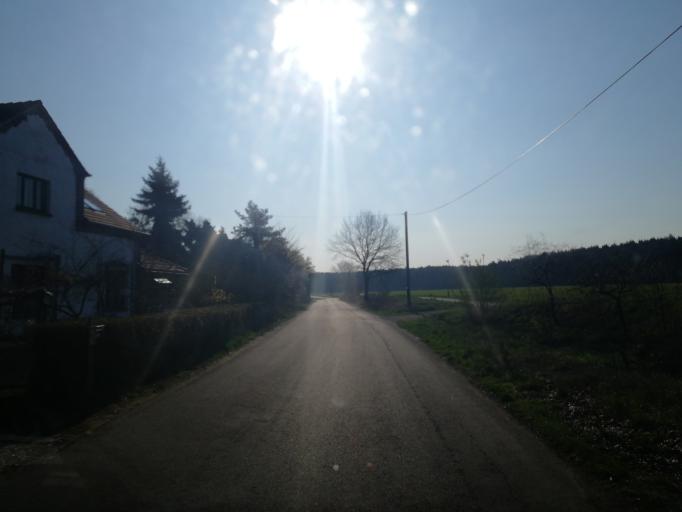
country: DE
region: Brandenburg
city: Drahnsdorf
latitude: 51.8954
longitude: 13.5623
